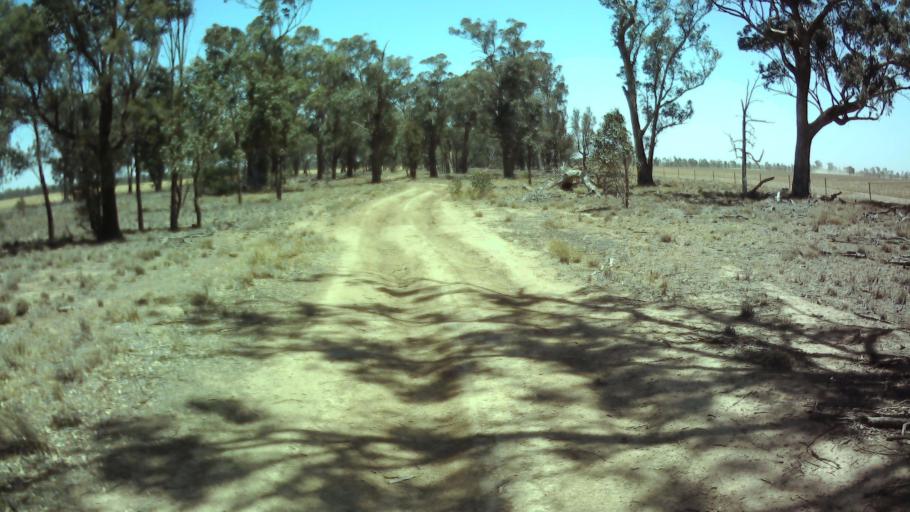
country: AU
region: New South Wales
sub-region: Weddin
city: Grenfell
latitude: -34.0540
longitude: 147.8240
